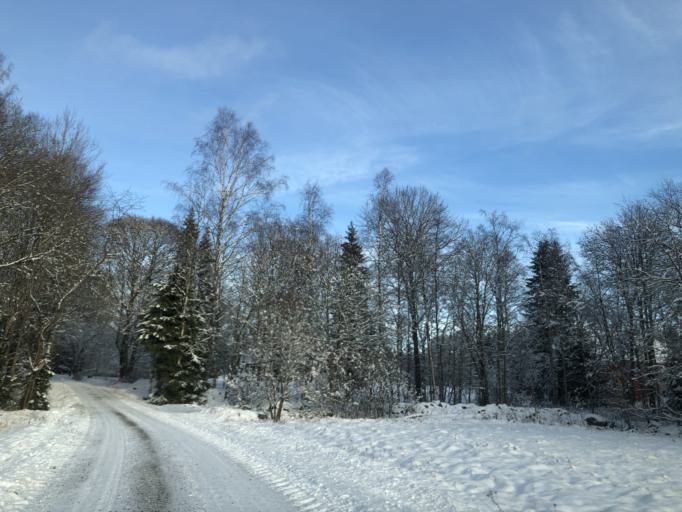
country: SE
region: Vaestra Goetaland
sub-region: Ulricehamns Kommun
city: Ulricehamn
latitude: 57.7450
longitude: 13.5070
